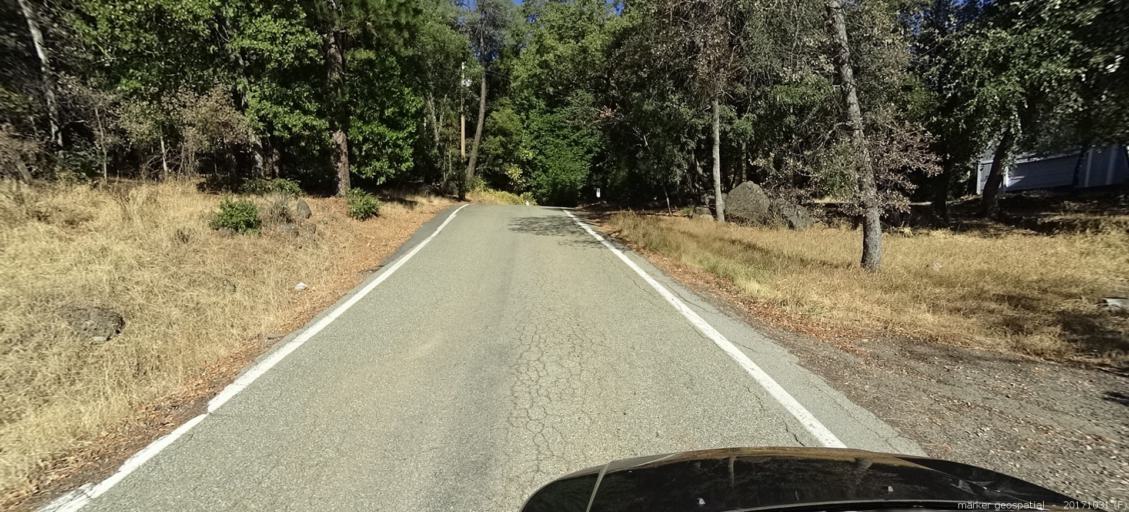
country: US
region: California
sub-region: Shasta County
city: Shingletown
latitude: 40.4614
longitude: -121.8917
